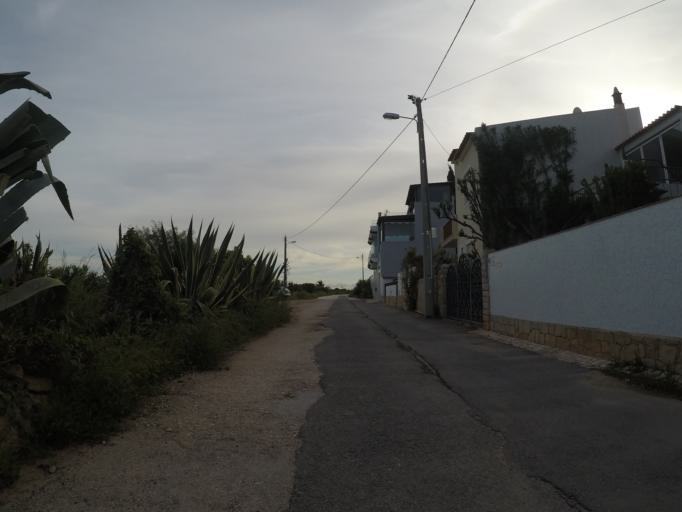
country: PT
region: Faro
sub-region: Lagos
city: Lagos
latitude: 37.0847
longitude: -8.7333
